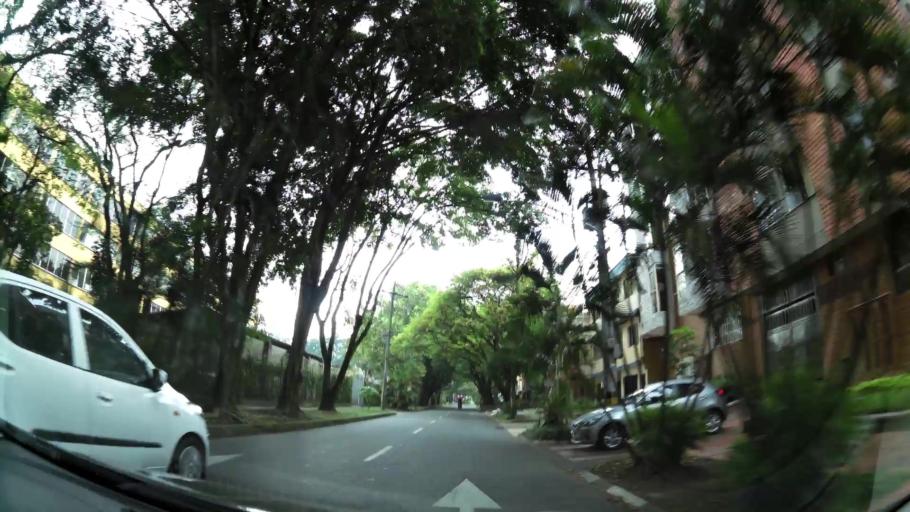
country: CO
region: Antioquia
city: Medellin
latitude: 6.2543
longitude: -75.5857
